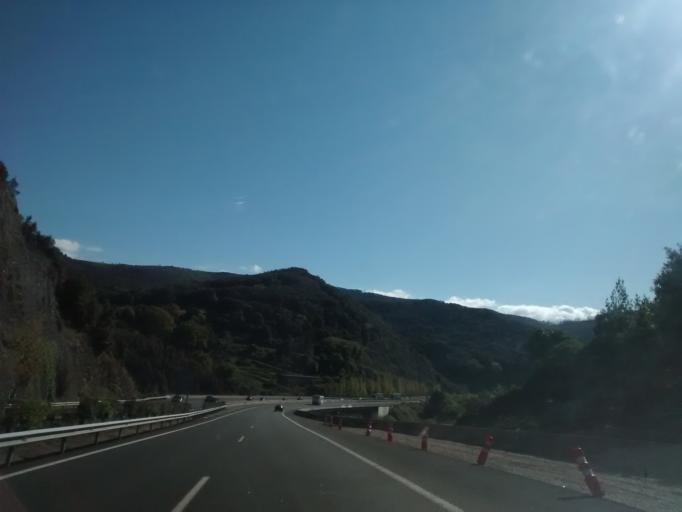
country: ES
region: Cantabria
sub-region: Provincia de Cantabria
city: Liendo
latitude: 43.3841
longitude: -3.3648
